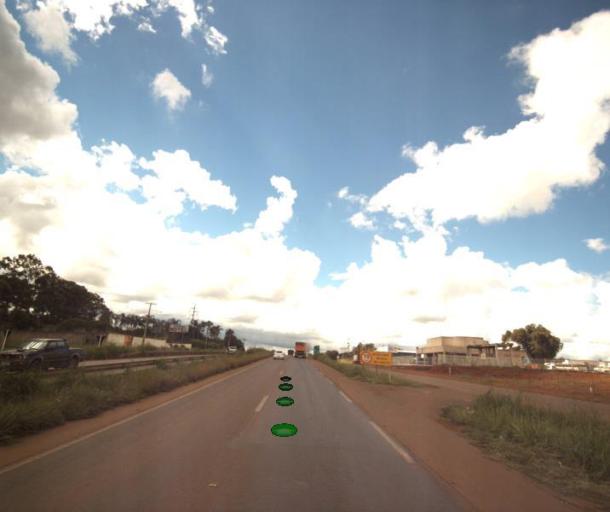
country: BR
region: Goias
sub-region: Anapolis
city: Anapolis
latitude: -16.3612
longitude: -48.9329
